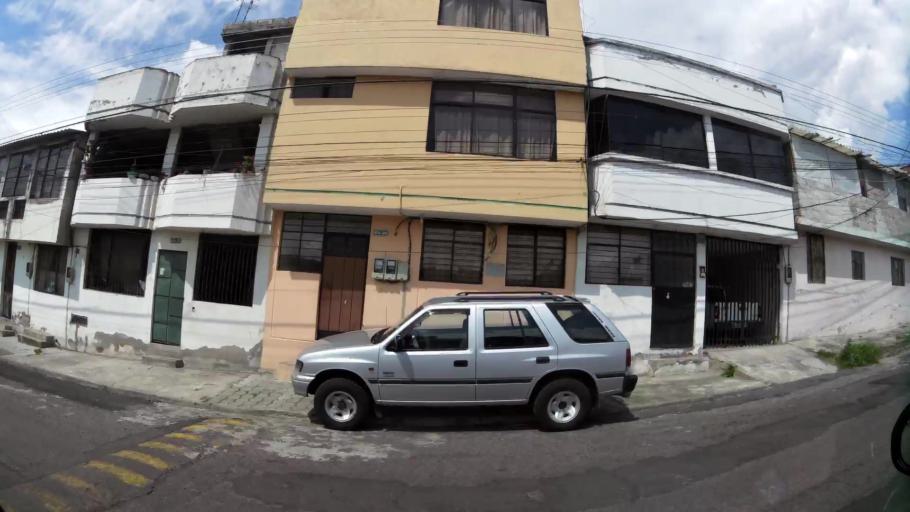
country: EC
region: Pichincha
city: Quito
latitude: -0.0896
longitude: -78.4541
